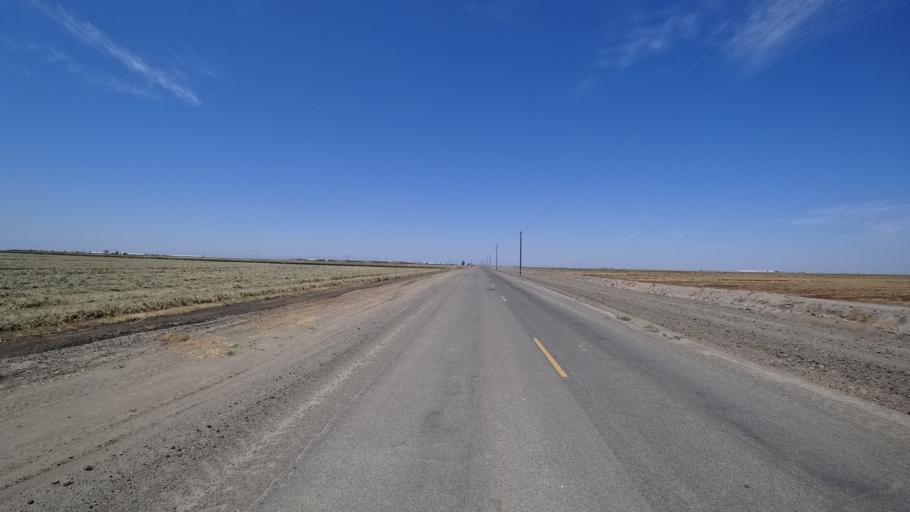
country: US
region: California
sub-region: Kings County
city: Corcoran
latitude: 36.1379
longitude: -119.6564
